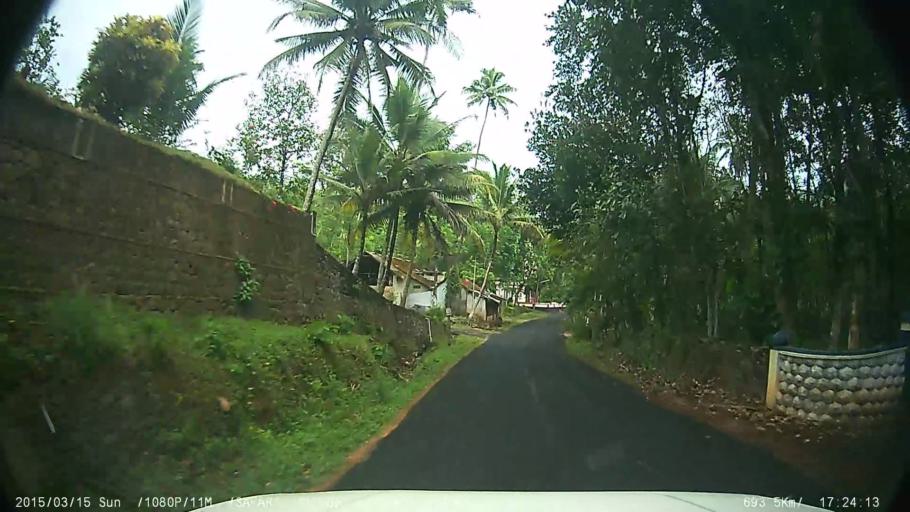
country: IN
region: Kerala
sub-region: Kottayam
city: Lalam
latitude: 9.8305
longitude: 76.7170
